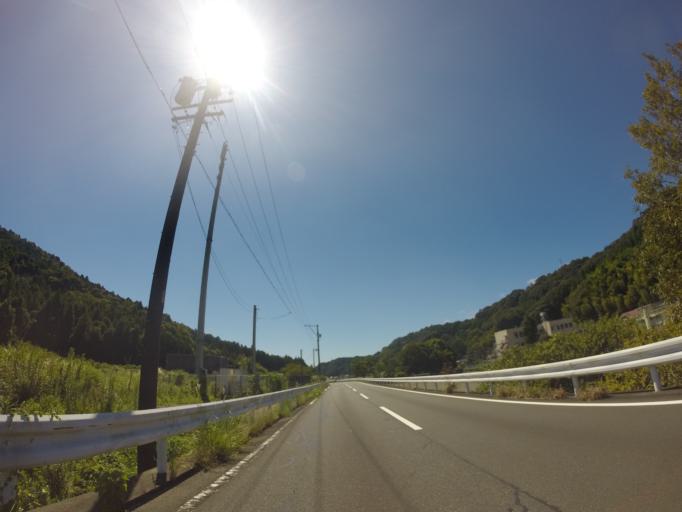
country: JP
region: Shizuoka
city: Kanaya
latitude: 34.8734
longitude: 138.1359
